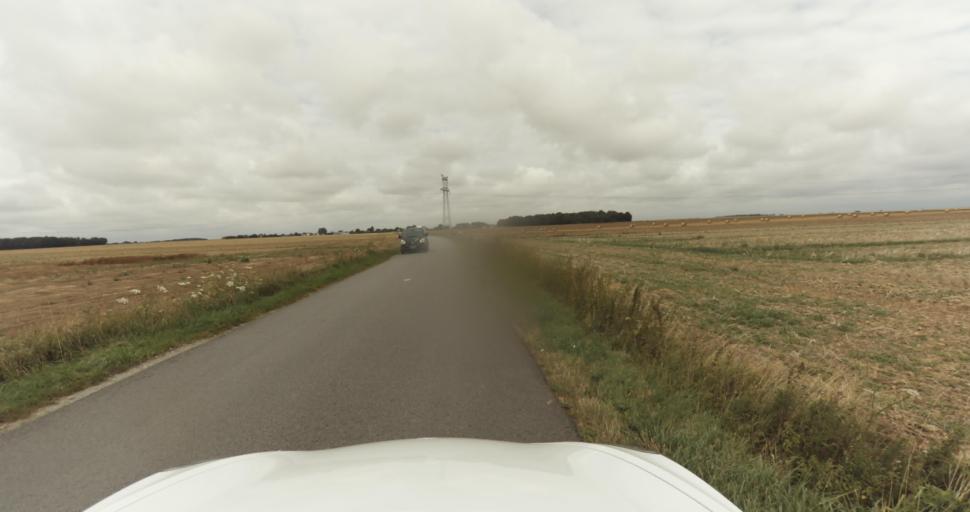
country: FR
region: Haute-Normandie
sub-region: Departement de l'Eure
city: Claville
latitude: 49.0340
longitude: 1.0293
